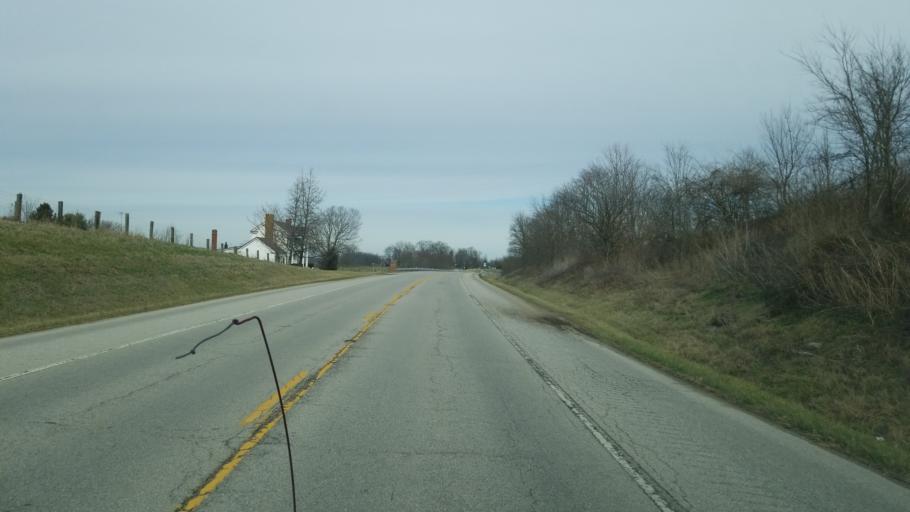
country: US
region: Kentucky
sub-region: Fleming County
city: Flemingsburg
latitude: 38.5033
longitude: -83.8511
